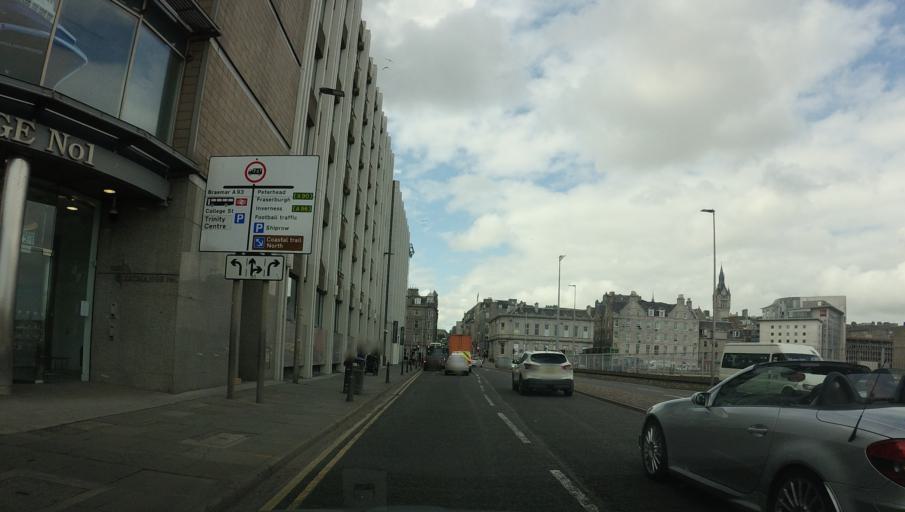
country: GB
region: Scotland
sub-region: Aberdeen City
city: Aberdeen
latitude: 57.1443
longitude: -2.0950
